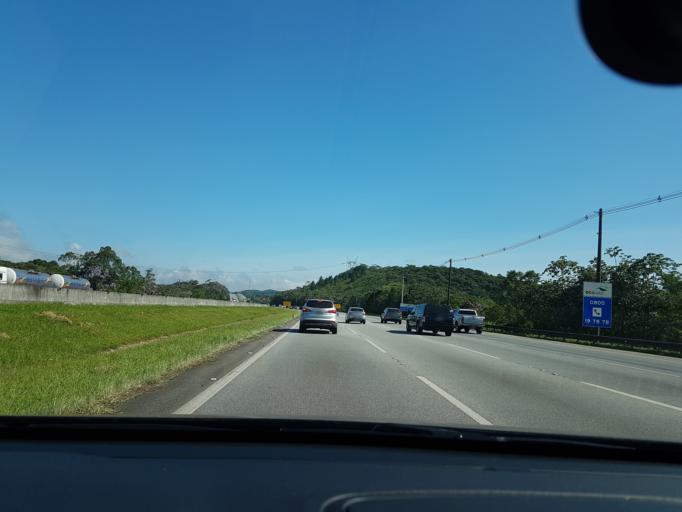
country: BR
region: Sao Paulo
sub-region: Cubatao
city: Cubatao
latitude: -23.8644
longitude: -46.5737
